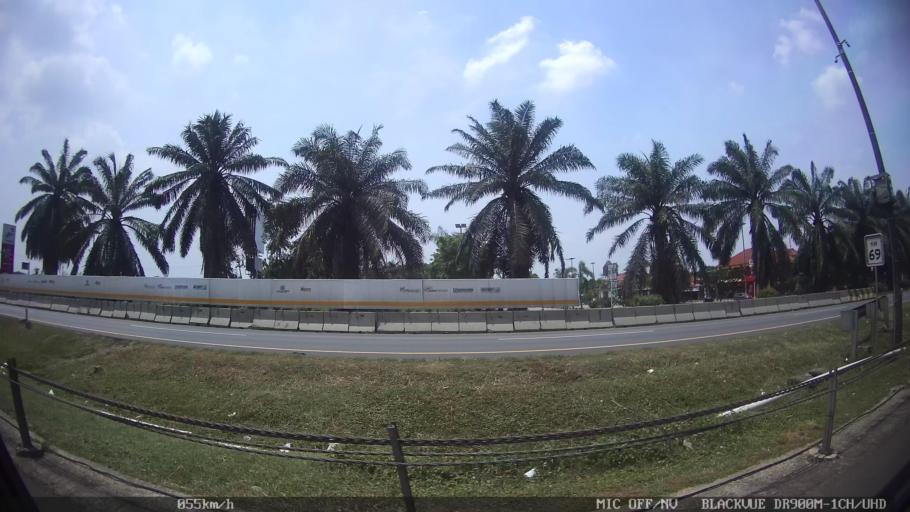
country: ID
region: Banten
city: Serang
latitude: -6.1321
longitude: 106.2041
